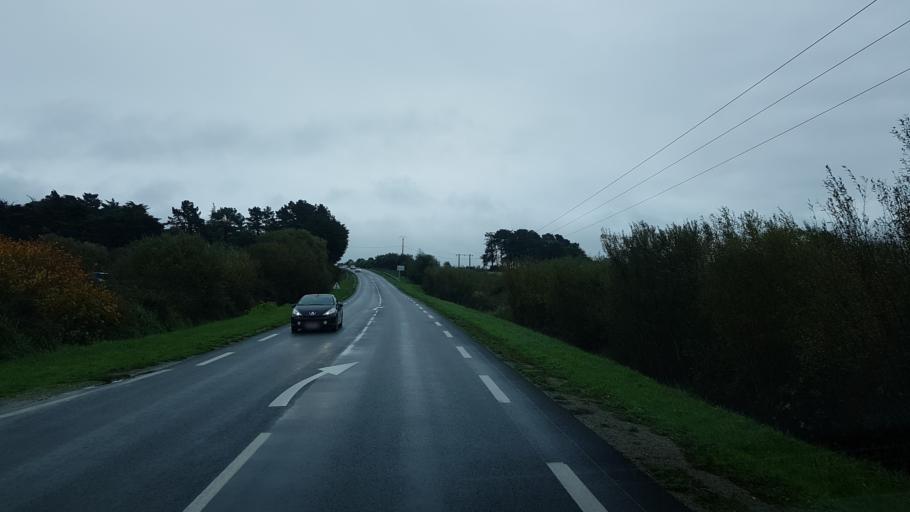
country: FR
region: Brittany
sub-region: Departement du Morbihan
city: Saint-Gildas-de-Rhuys
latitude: 47.5335
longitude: -2.8531
